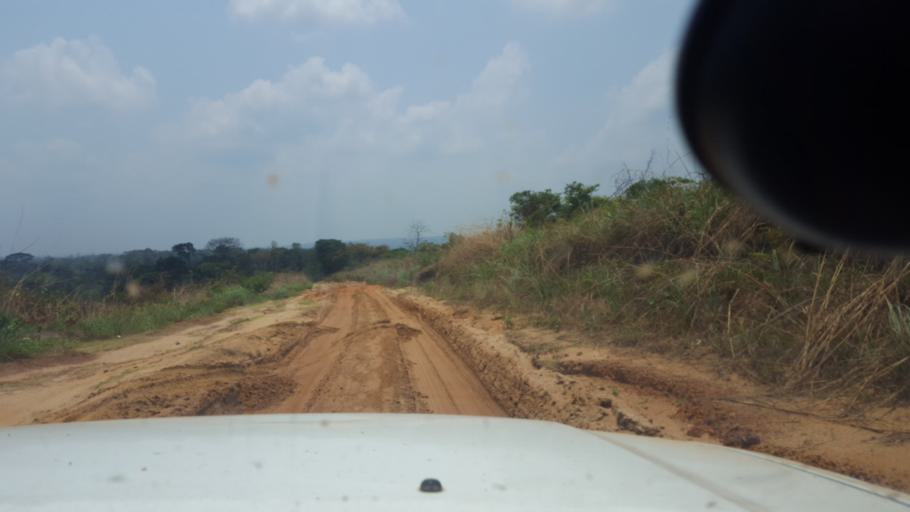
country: CD
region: Bandundu
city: Mushie
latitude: -3.7564
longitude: 16.6249
